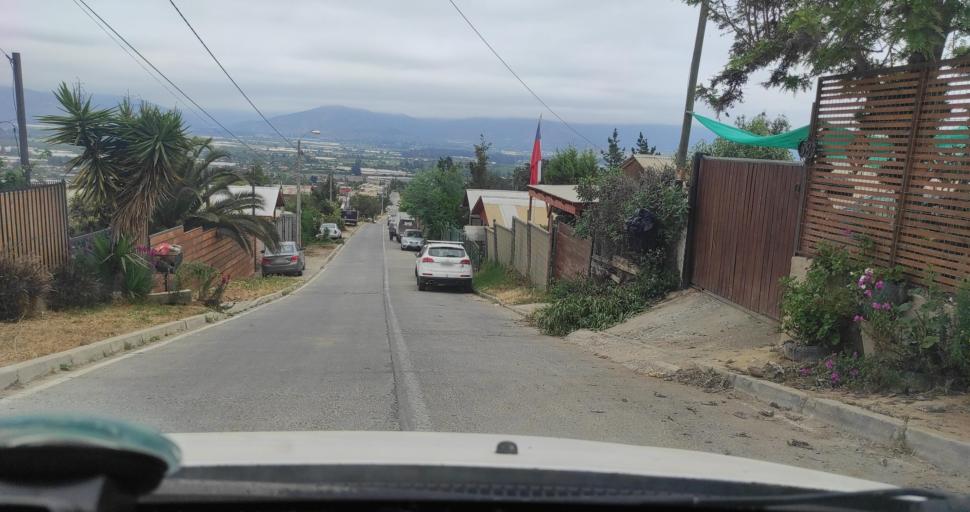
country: CL
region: Valparaiso
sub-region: Provincia de Marga Marga
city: Limache
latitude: -32.9849
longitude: -71.2244
